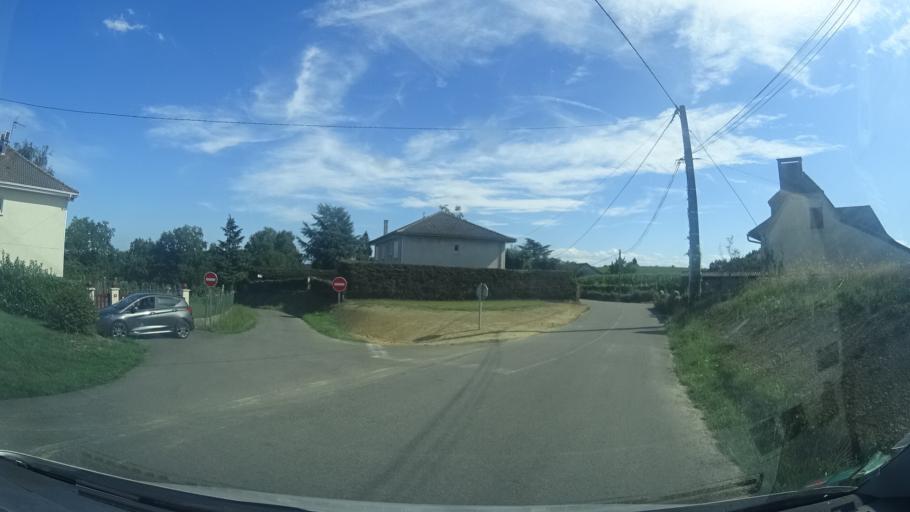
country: FR
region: Aquitaine
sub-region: Departement des Pyrenees-Atlantiques
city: Mont
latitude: 43.4925
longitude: -0.6642
